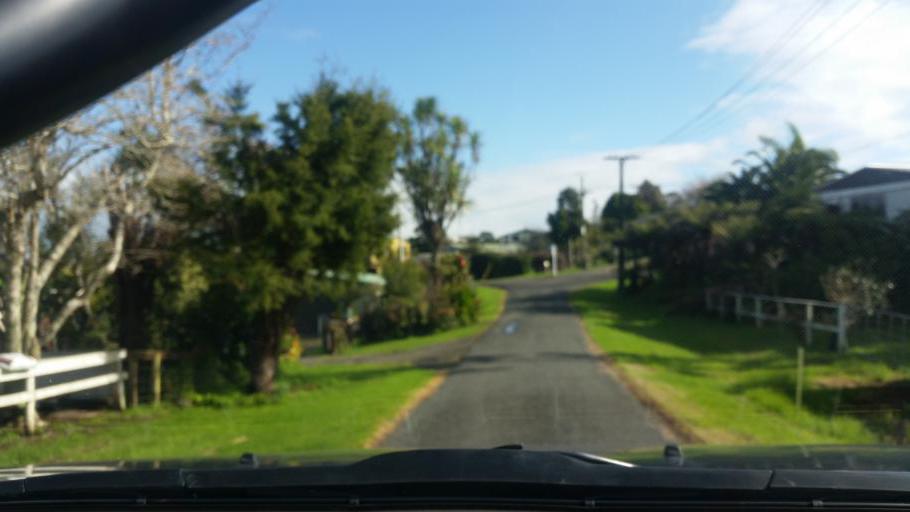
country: NZ
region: Auckland
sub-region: Auckland
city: Wellsford
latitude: -36.2469
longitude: 174.2488
